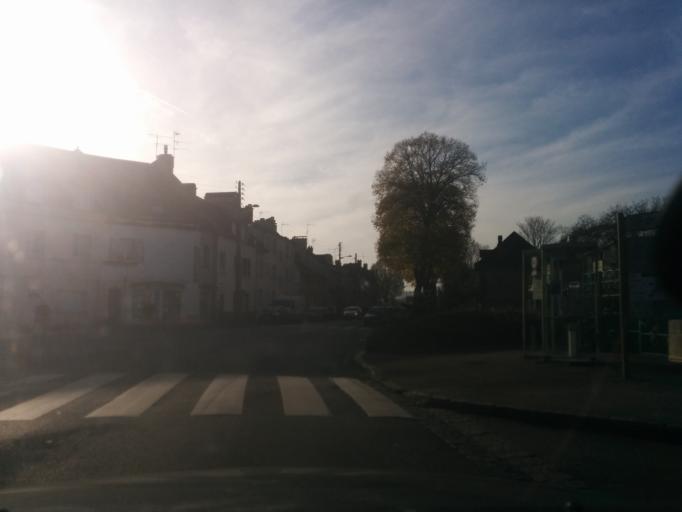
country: FR
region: Haute-Normandie
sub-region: Departement de l'Eure
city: Vernon
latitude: 49.0981
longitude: 1.4911
